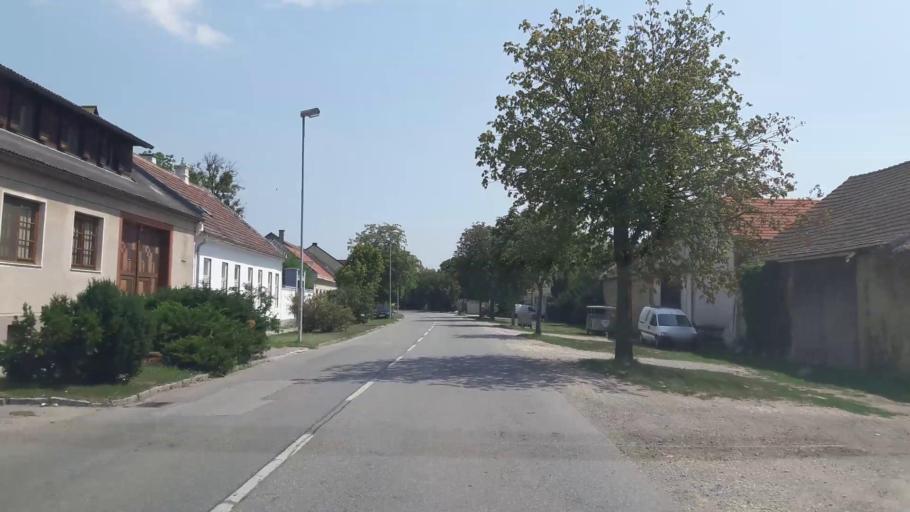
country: AT
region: Lower Austria
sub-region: Politischer Bezirk Bruck an der Leitha
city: Trautmannsdorf an der Leitha
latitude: 48.0233
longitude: 16.6358
